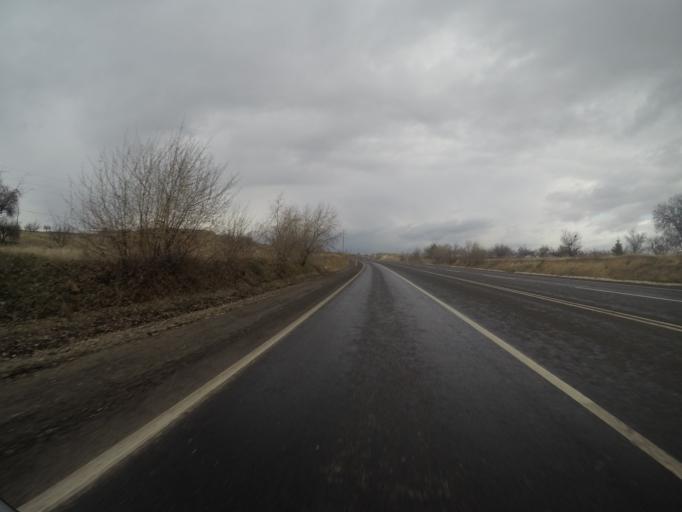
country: TR
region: Nevsehir
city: Goereme
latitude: 38.6351
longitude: 34.8728
